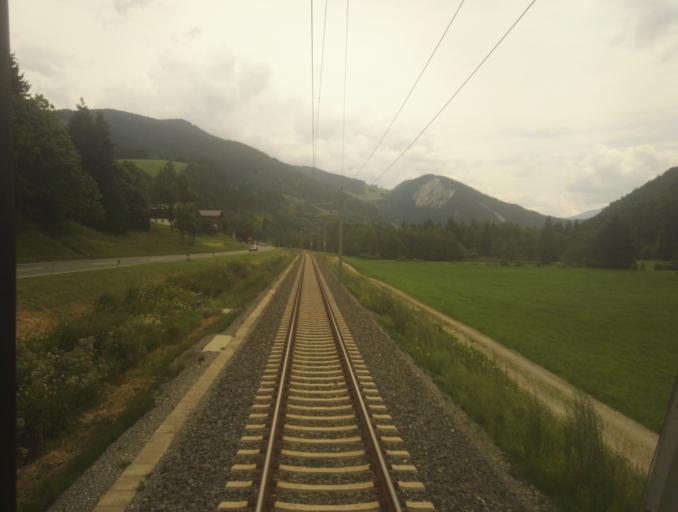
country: AT
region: Salzburg
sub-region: Politischer Bezirk Sankt Johann im Pongau
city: Forstau
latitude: 47.4014
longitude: 13.5512
